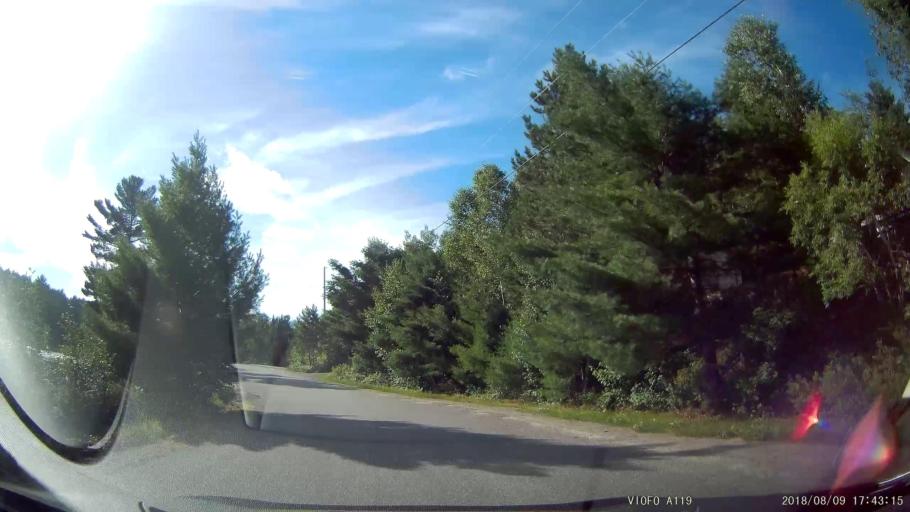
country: CA
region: Ontario
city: Rayside-Balfour
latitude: 46.6066
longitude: -81.5269
